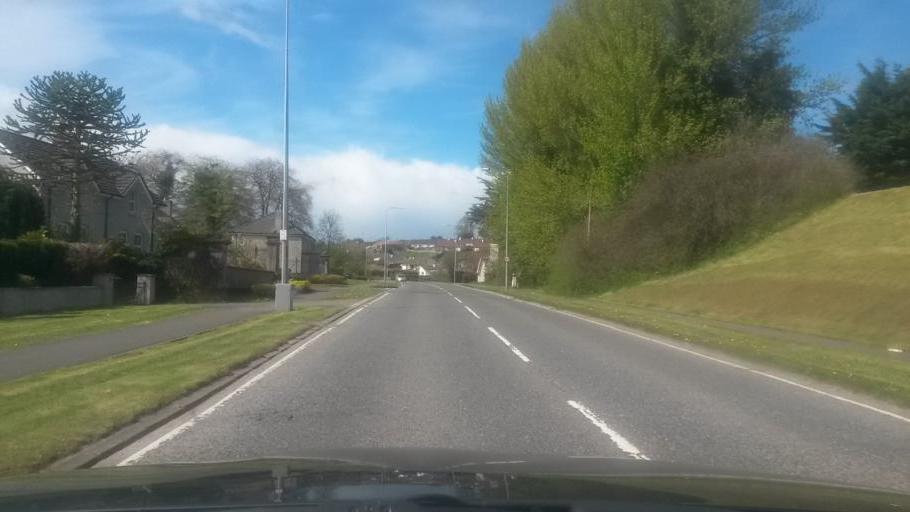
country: GB
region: Northern Ireland
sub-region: Fermanagh District
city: Enniskillen
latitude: 54.3591
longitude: -7.6720
